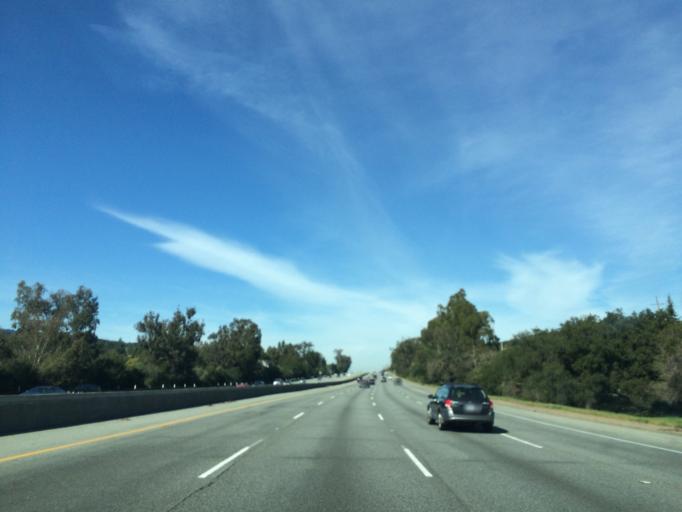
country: US
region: California
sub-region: San Mateo County
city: Emerald Lake Hills
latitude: 37.4456
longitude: -122.2715
